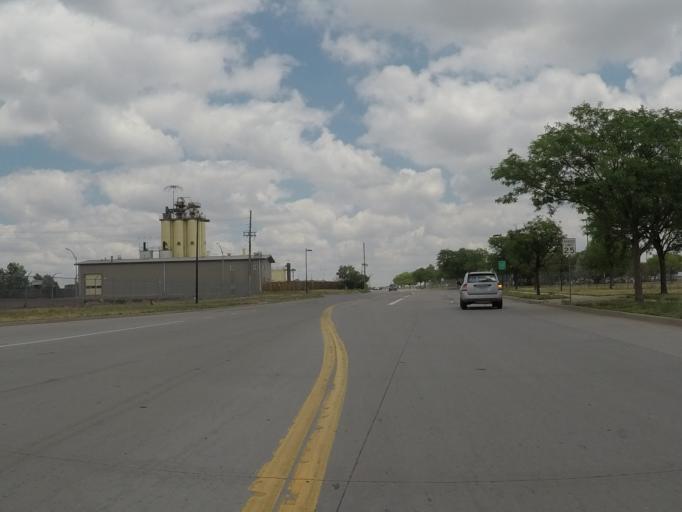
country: US
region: Colorado
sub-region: Adams County
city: Commerce City
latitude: 39.7935
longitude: -104.9028
